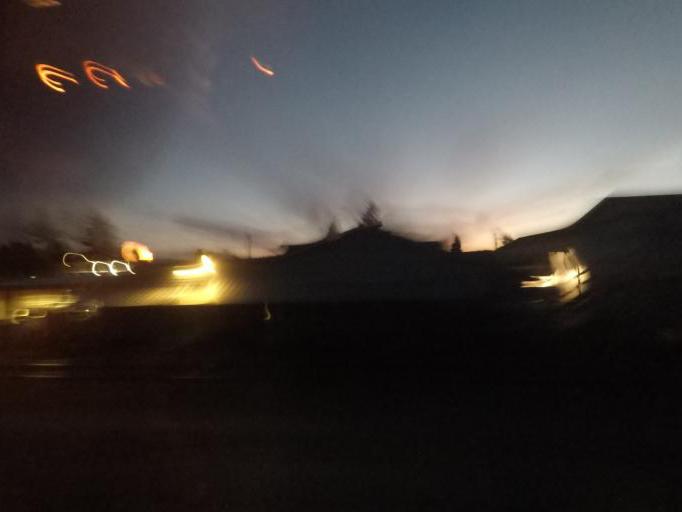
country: US
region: Washington
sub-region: Snohomish County
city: Marysville
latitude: 48.0552
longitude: -122.1796
